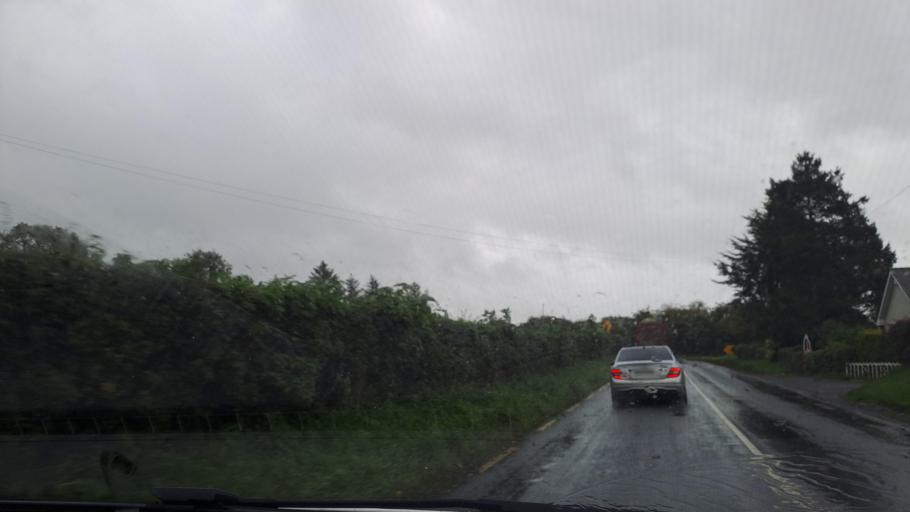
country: IE
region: Ulster
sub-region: County Monaghan
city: Carrickmacross
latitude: 53.9761
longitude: -6.6454
